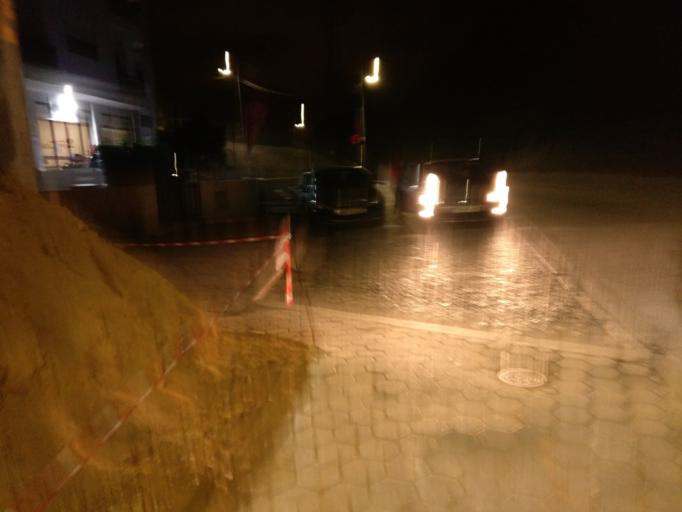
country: PT
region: Porto
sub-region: Vila Nova de Gaia
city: Vilar de Andorinho
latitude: 41.1096
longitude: -8.6033
